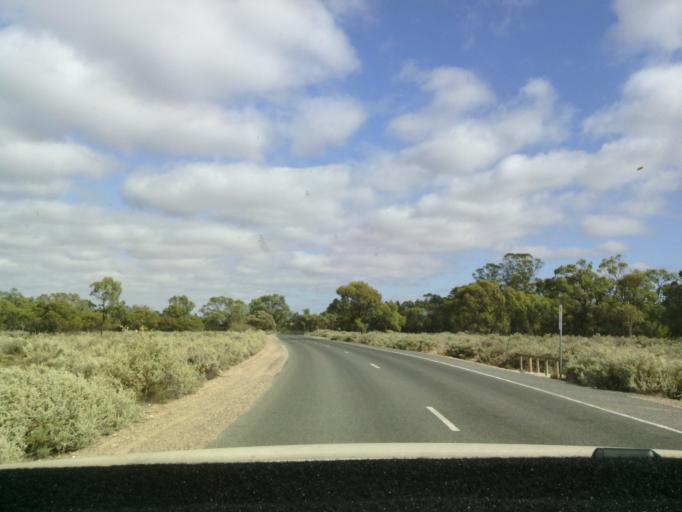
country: AU
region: South Australia
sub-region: Berri and Barmera
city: Berri
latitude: -34.2831
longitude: 140.6293
